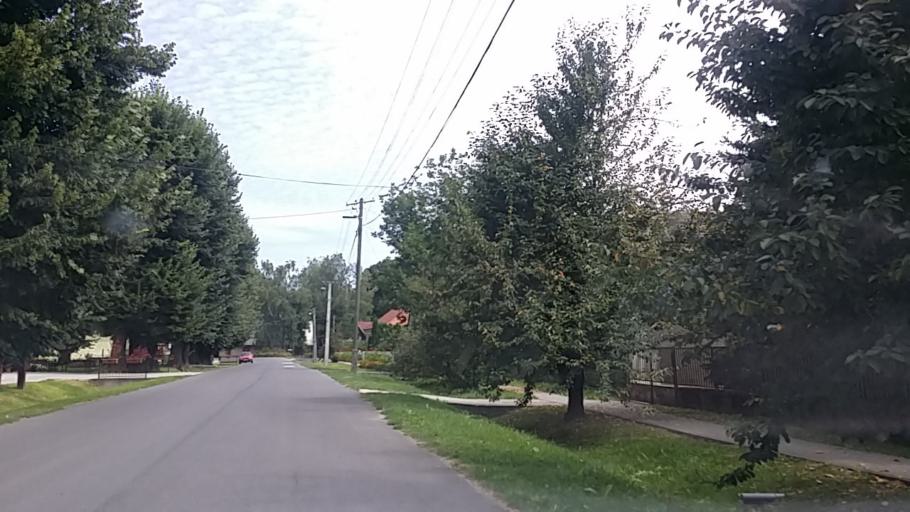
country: HU
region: Somogy
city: Taszar
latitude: 46.3543
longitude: 17.9903
